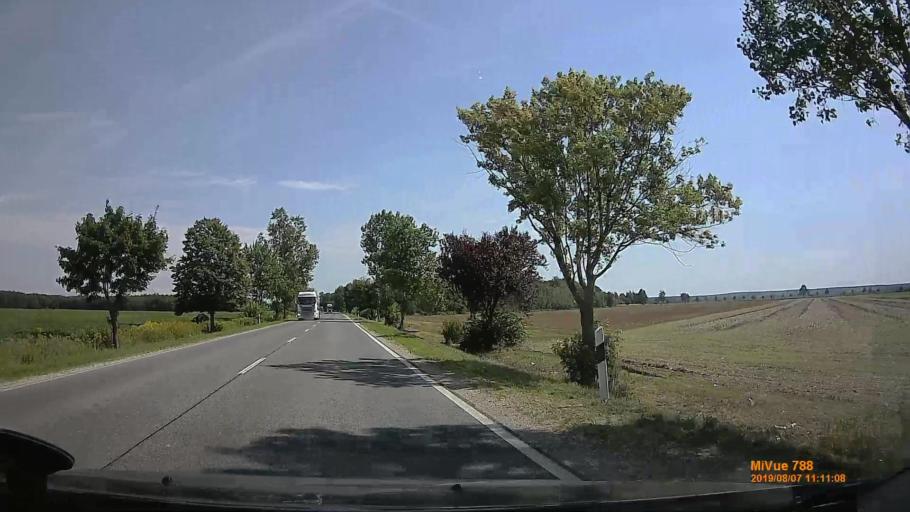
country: HU
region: Zala
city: Lenti
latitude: 46.6747
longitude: 16.5197
